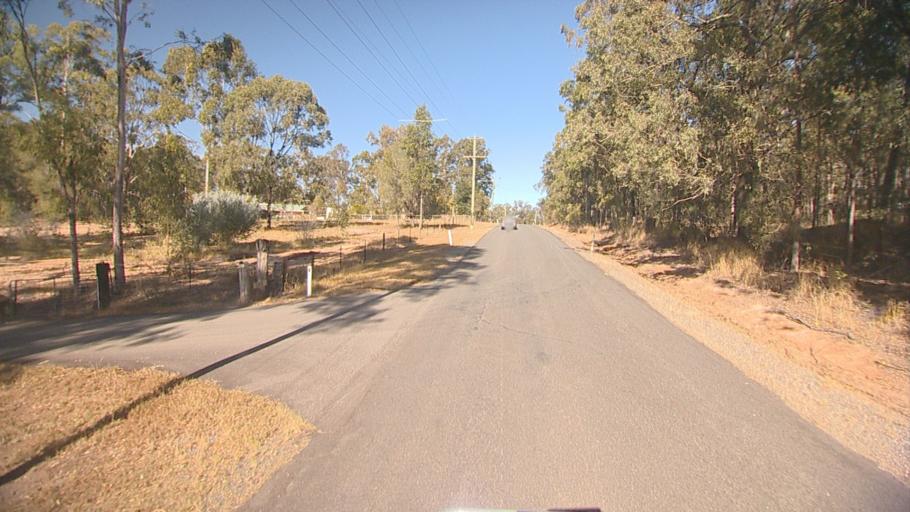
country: AU
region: Queensland
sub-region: Logan
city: Cedar Vale
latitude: -27.8533
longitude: 152.9936
